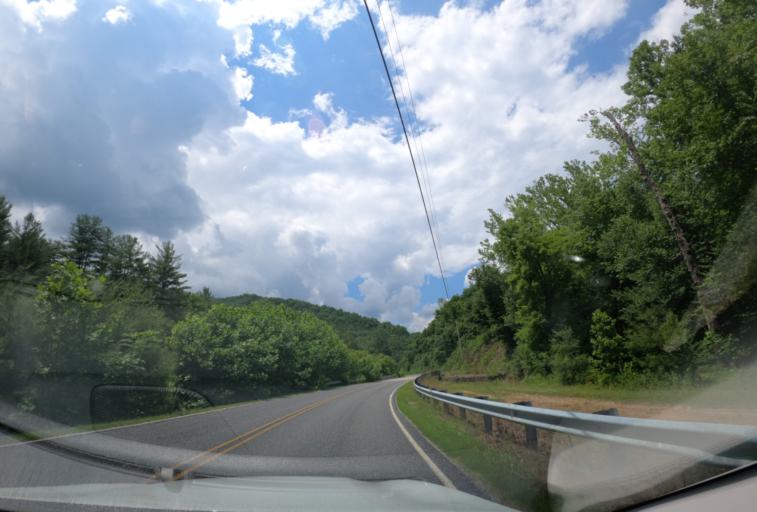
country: US
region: North Carolina
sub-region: Haywood County
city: Hazelwood
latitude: 35.4057
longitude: -82.9022
